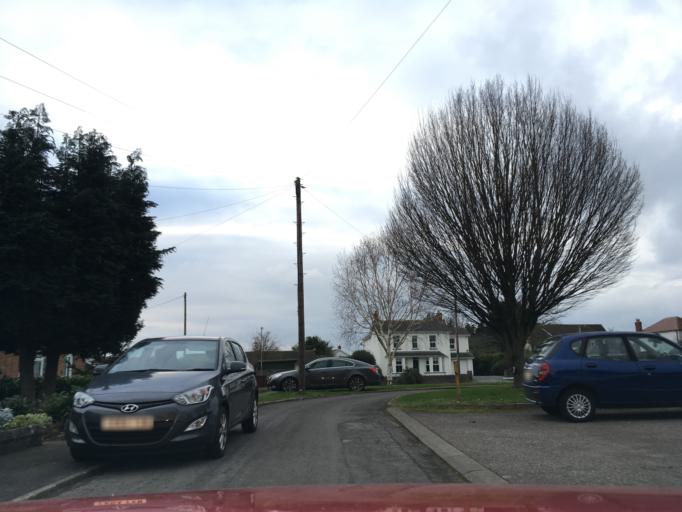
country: GB
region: Wales
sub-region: Monmouthshire
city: Magor
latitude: 51.5835
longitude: -2.8323
